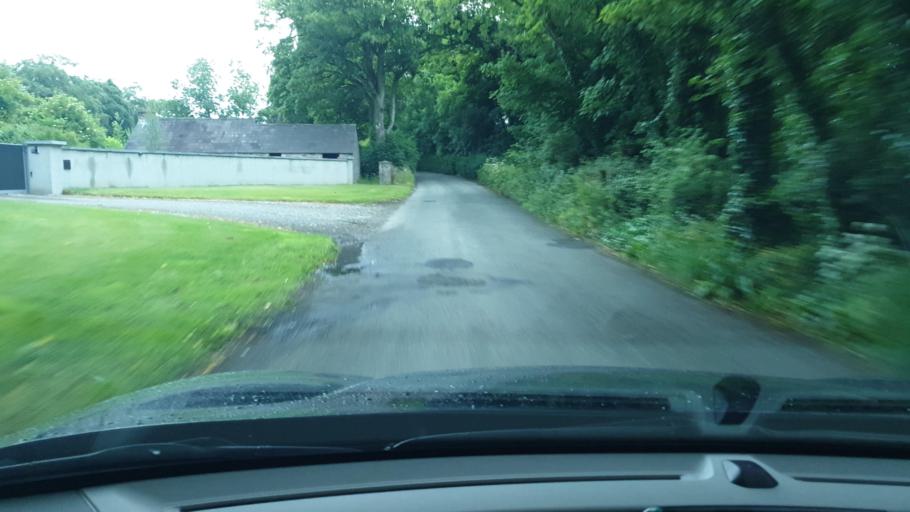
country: IE
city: Kentstown
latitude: 53.5999
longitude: -6.5963
